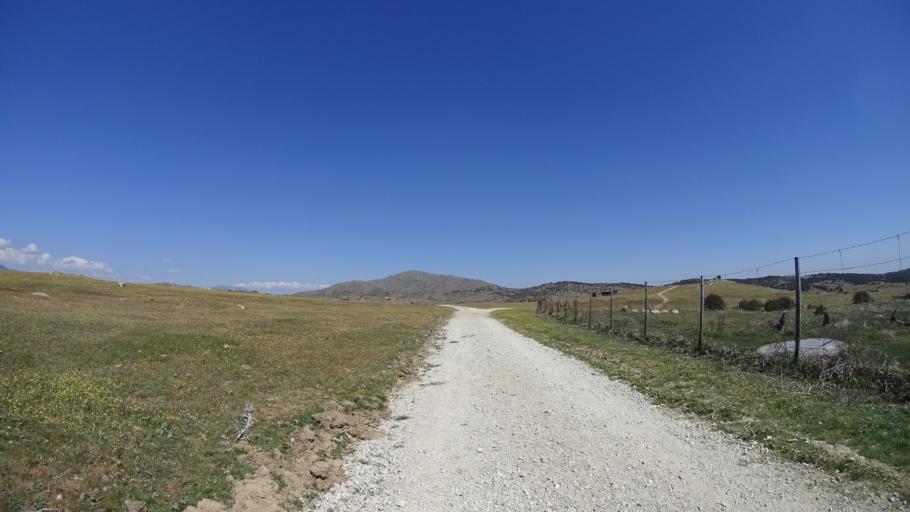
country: ES
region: Madrid
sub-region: Provincia de Madrid
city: Colmenar Viejo
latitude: 40.6896
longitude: -3.7544
